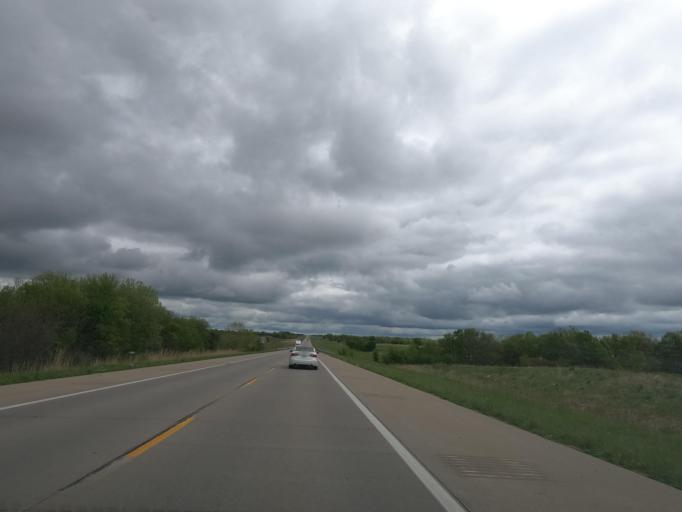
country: US
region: Kansas
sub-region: Montgomery County
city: Cherryvale
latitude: 37.3470
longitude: -95.5590
